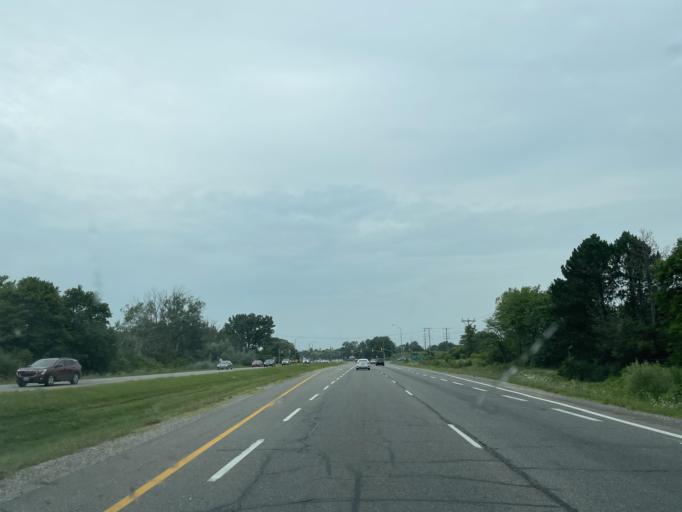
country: CA
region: Ontario
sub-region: Wellington County
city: Guelph
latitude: 43.5114
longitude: -80.2406
